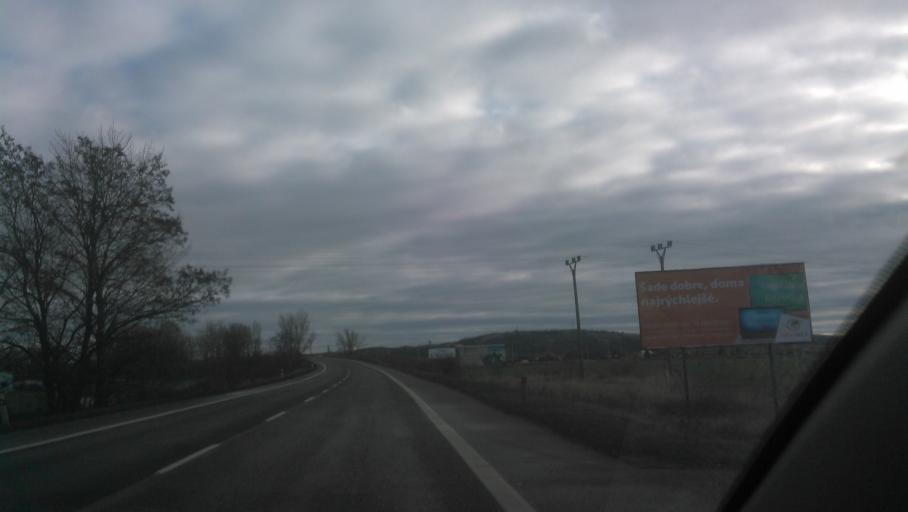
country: SK
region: Trnavsky
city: Leopoldov
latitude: 48.4362
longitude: 17.7514
